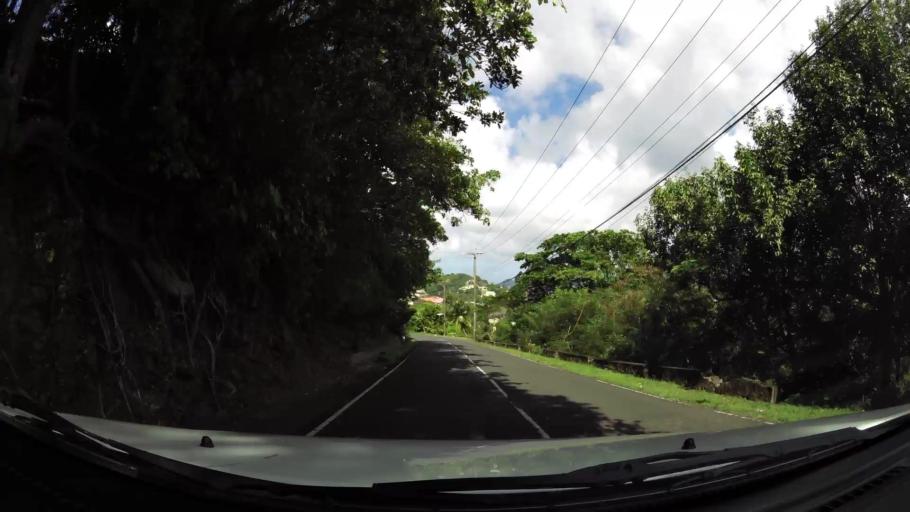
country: LC
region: Castries Quarter
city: Castries
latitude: 14.0107
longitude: -61.0045
